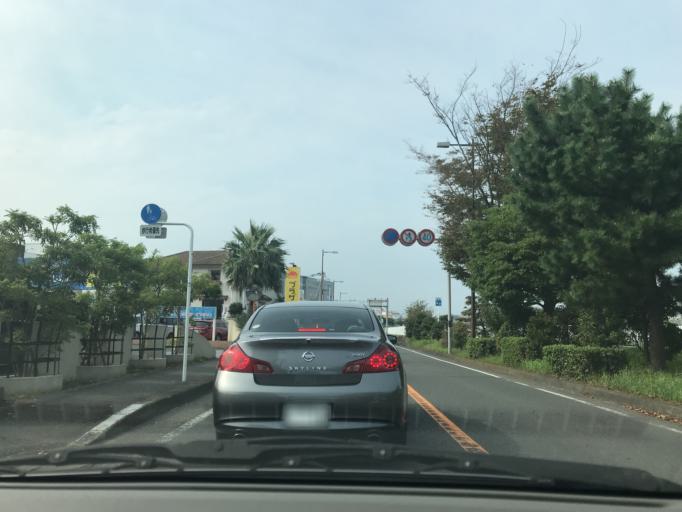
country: JP
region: Kanagawa
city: Fujisawa
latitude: 35.3388
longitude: 139.4681
